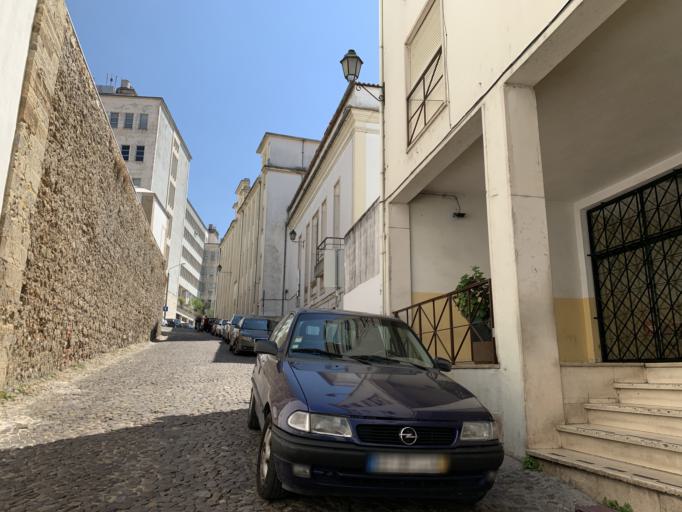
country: PT
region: Coimbra
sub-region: Coimbra
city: Coimbra
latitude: 40.2067
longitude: -8.4253
